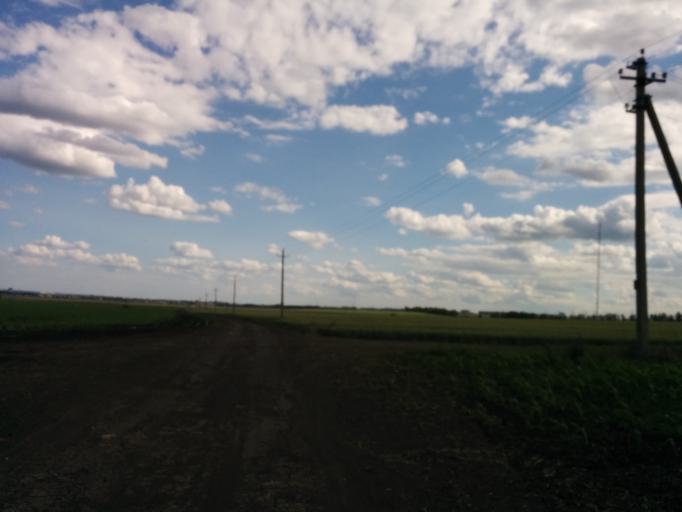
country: RU
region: Tambov
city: Donskoye
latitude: 52.7989
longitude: 41.4262
